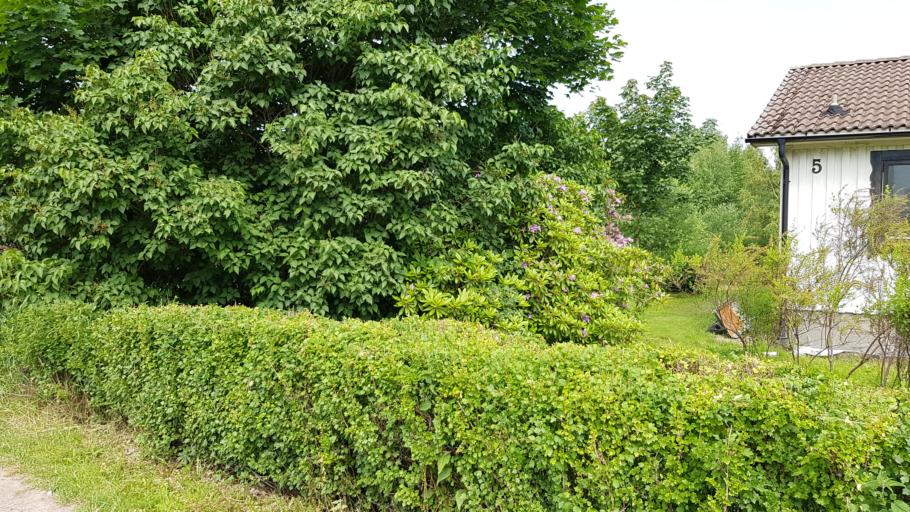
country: SE
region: Vaermland
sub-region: Karlstads Kommun
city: Karlstad
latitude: 59.3347
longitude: 13.5476
